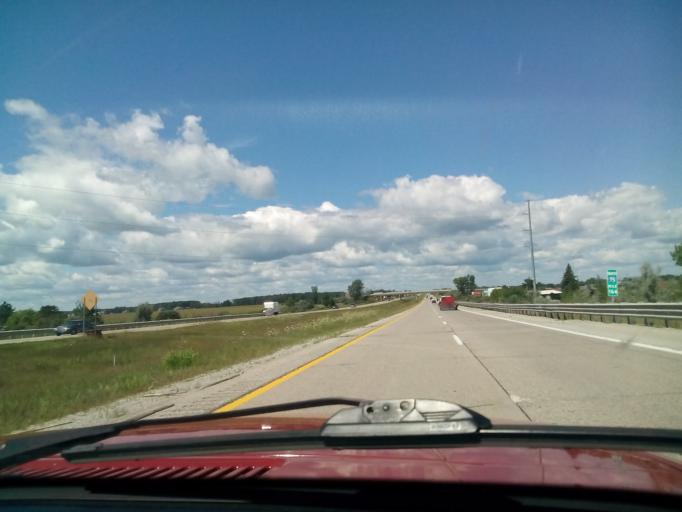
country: US
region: Michigan
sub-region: Bay County
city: Bay City
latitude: 43.6207
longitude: -83.9502
